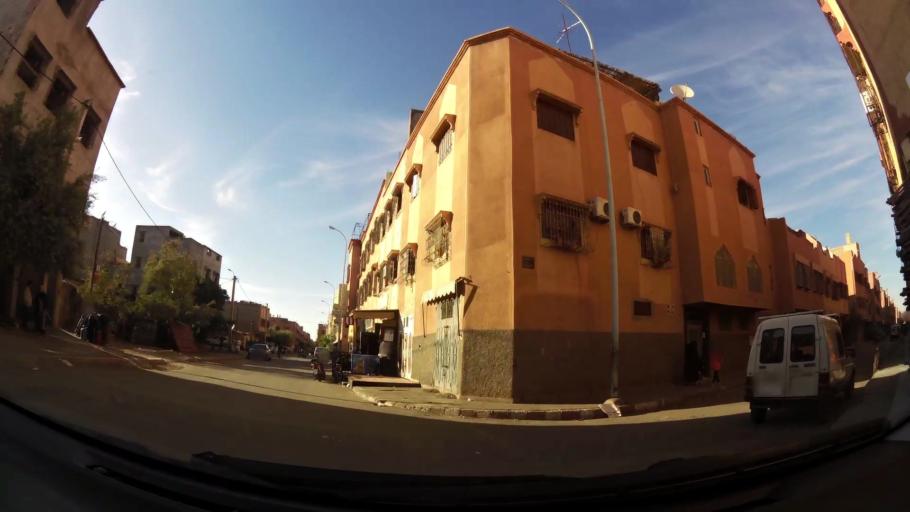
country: MA
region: Marrakech-Tensift-Al Haouz
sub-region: Marrakech
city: Marrakesh
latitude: 31.6177
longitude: -8.0669
